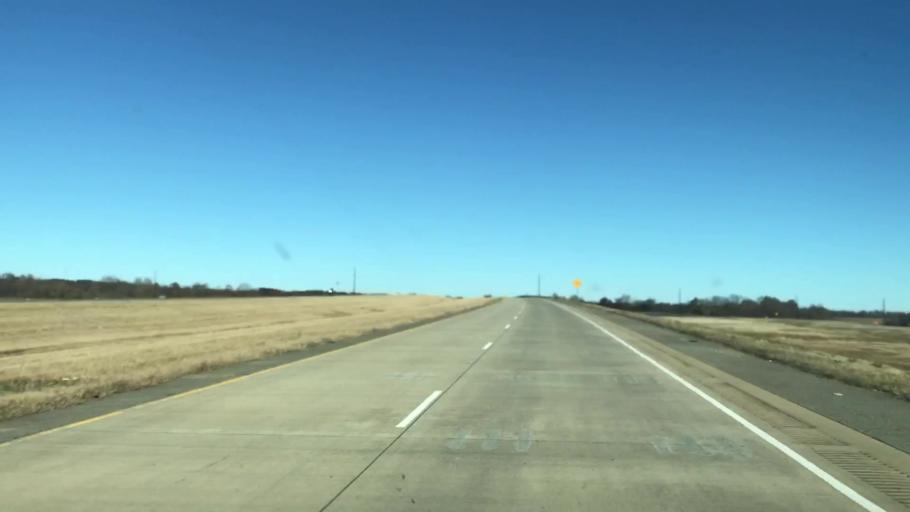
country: US
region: Louisiana
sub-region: Caddo Parish
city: Vivian
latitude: 32.8939
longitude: -93.8605
